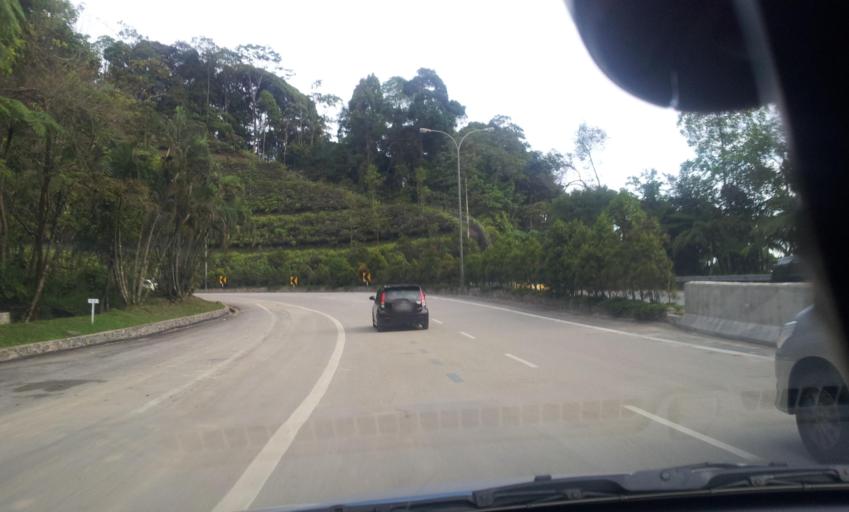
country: MY
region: Pahang
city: Kampung Bukit Tinggi, Bentong
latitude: 3.4029
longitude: 101.7859
